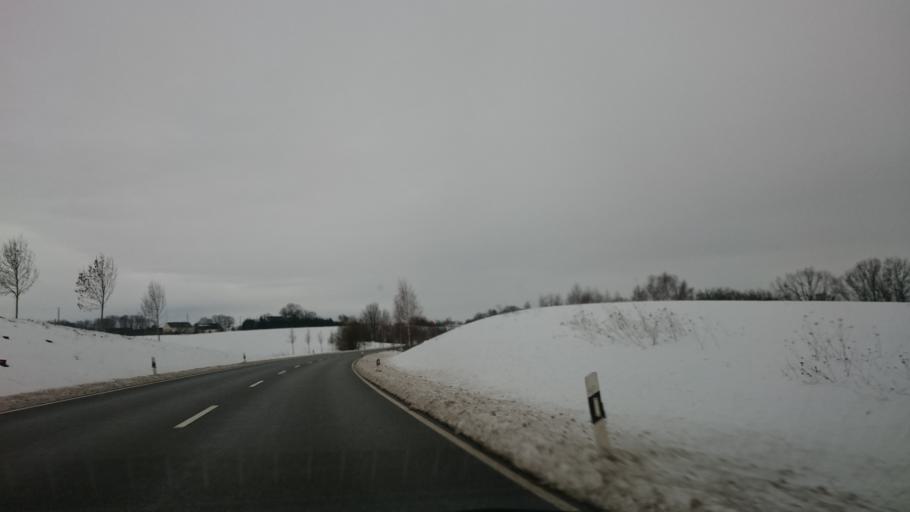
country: DE
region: Saxony
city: Lichtenstein
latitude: 50.7515
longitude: 12.6020
